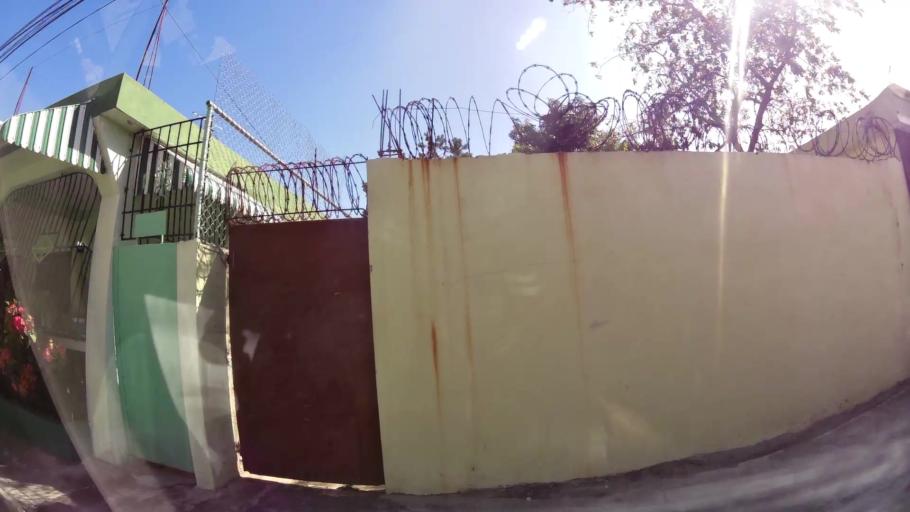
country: DO
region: San Cristobal
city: San Cristobal
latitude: 18.4324
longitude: -70.1203
